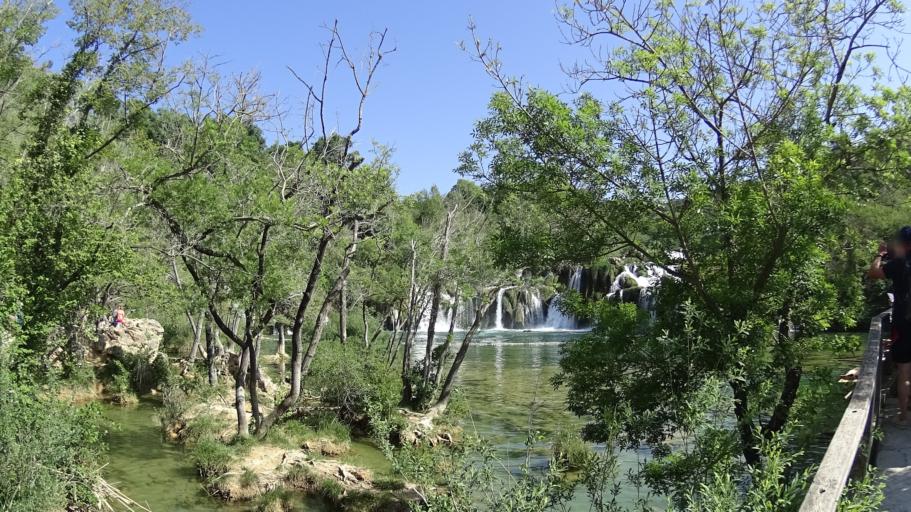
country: HR
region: Sibensko-Kniniska
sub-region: Grad Sibenik
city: Sibenik
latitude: 43.8059
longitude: 15.9635
